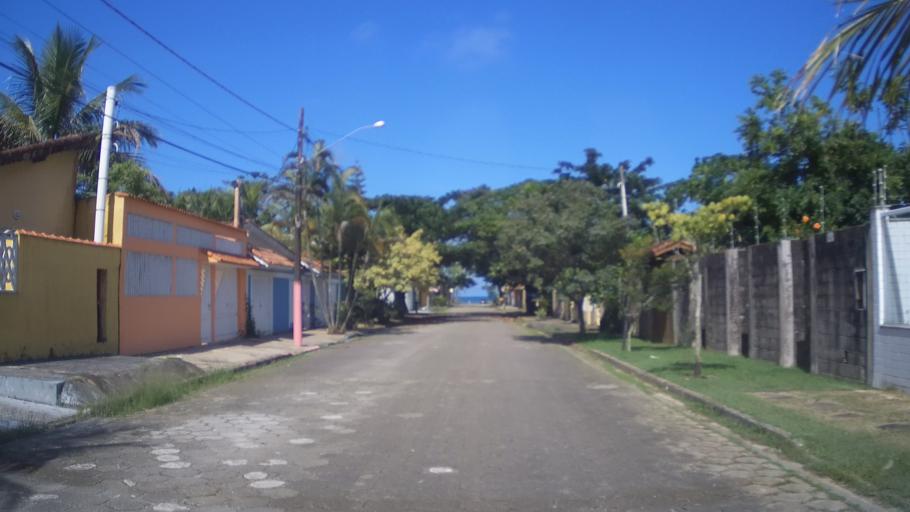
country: BR
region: Sao Paulo
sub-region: Itanhaem
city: Itanhaem
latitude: -24.1484
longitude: -46.7231
